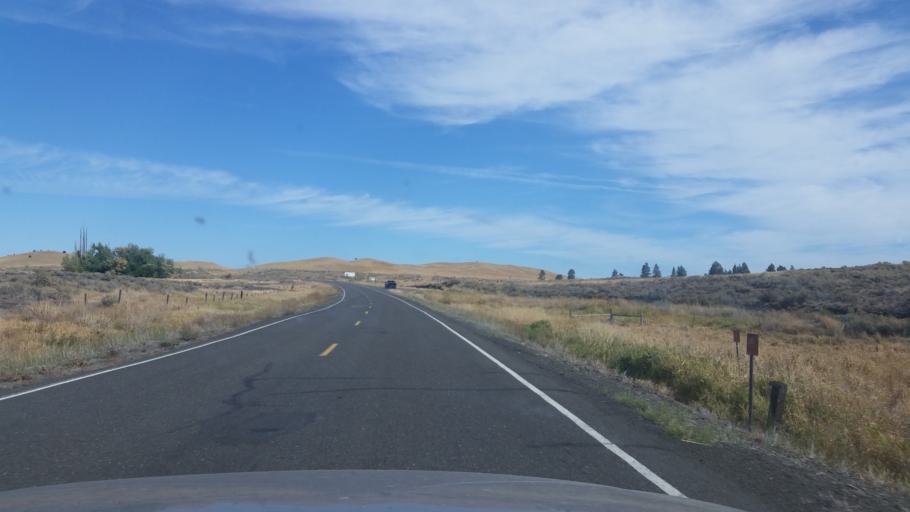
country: US
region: Washington
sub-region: Spokane County
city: Medical Lake
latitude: 47.3596
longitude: -117.8468
